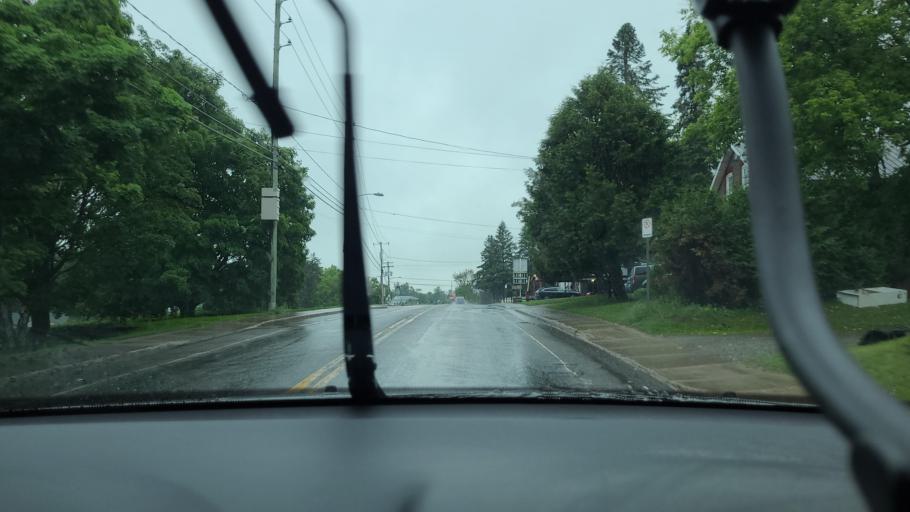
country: CA
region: Quebec
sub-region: Outaouais
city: Saint-Andre-Avellin
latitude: 45.7187
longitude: -75.0571
